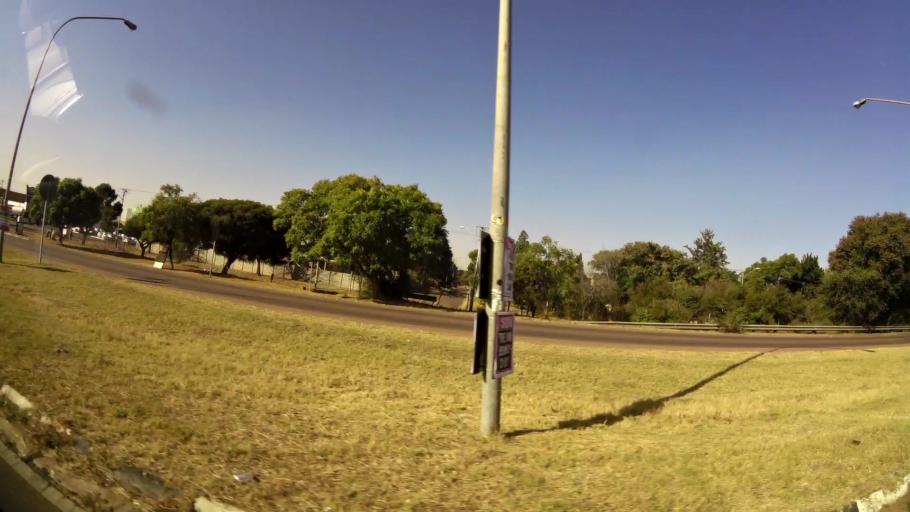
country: ZA
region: Gauteng
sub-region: City of Tshwane Metropolitan Municipality
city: Pretoria
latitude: -25.7213
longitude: 28.2580
